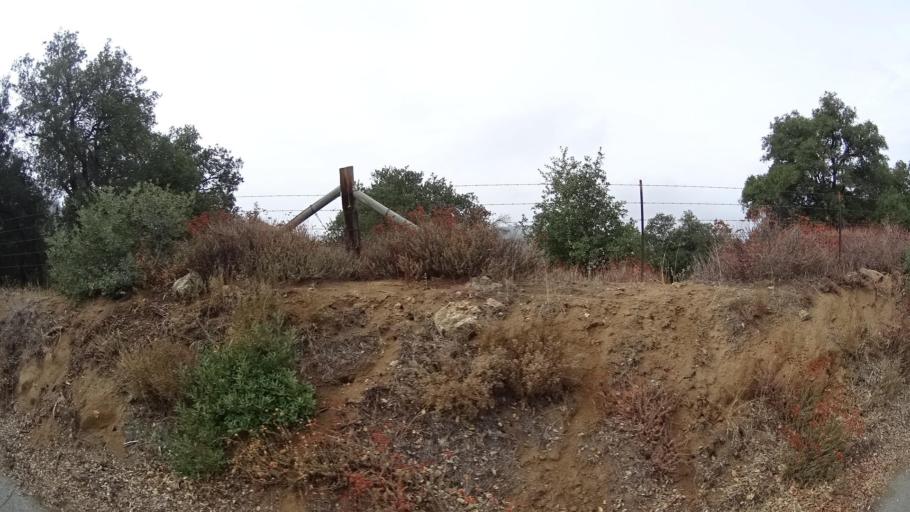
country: US
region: California
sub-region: San Diego County
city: Julian
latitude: 33.0616
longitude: -116.6089
